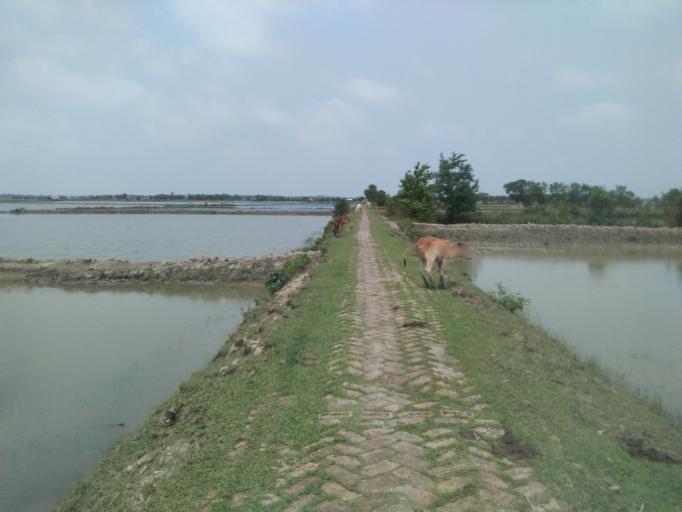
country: BD
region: Khulna
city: Phultala
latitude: 22.6425
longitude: 89.4183
